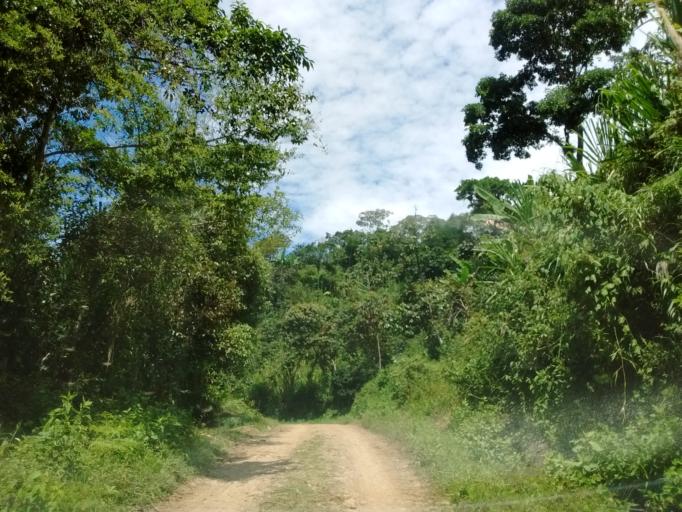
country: CO
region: Cauca
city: Morales
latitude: 2.6661
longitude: -76.7660
